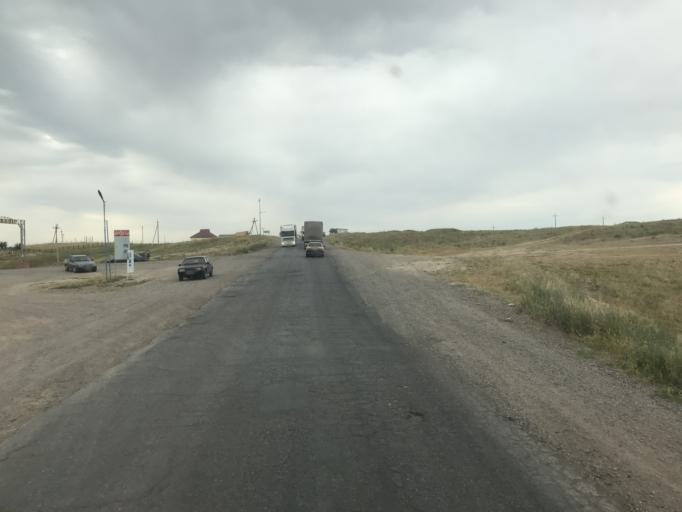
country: UZ
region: Toshkent
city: Chinoz
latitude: 41.1322
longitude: 68.7198
